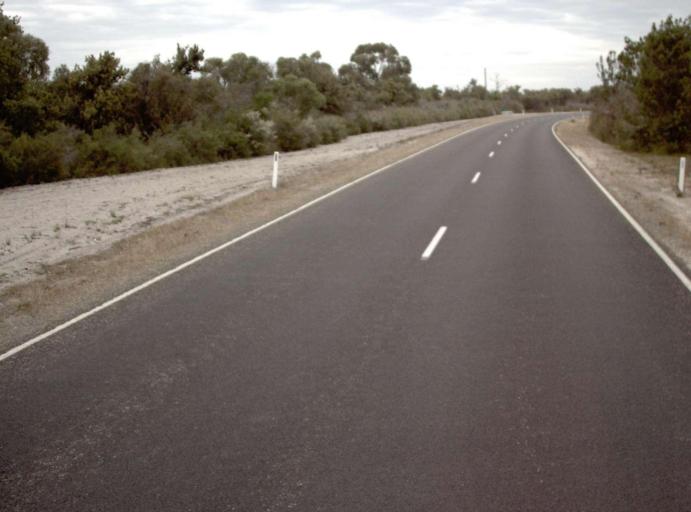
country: AU
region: Victoria
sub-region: Wellington
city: Sale
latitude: -38.1799
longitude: 147.3781
